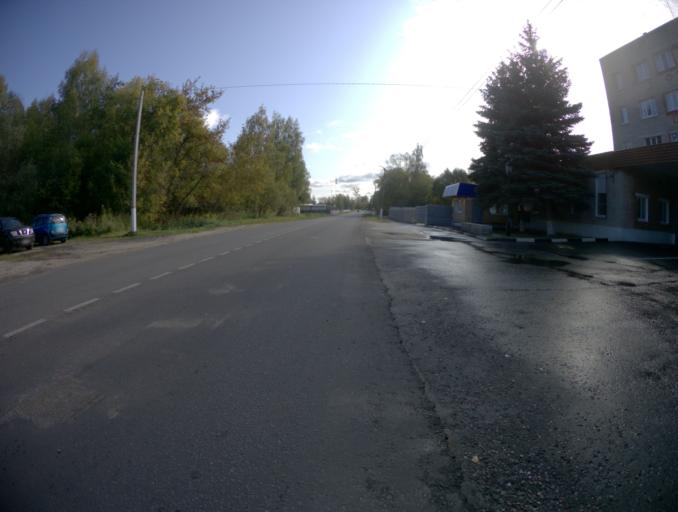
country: RU
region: Moskovskaya
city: Roshal'
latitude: 55.6601
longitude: 39.8820
